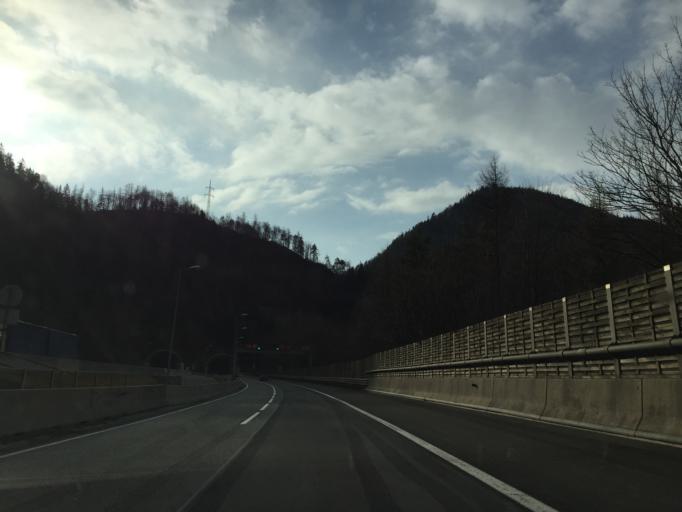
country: AT
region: Salzburg
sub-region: Politischer Bezirk Sankt Johann im Pongau
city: Werfen
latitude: 47.4949
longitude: 13.1809
